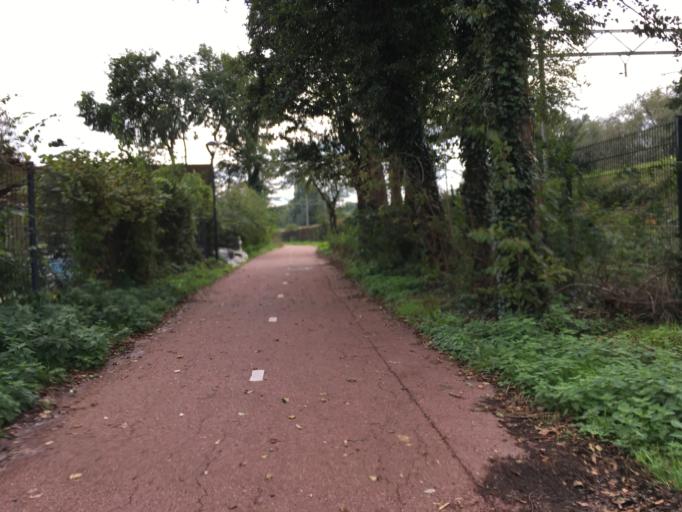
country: NL
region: North Holland
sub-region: Gemeente Bloemendaal
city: Bloemendaal
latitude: 52.3939
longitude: 4.6235
